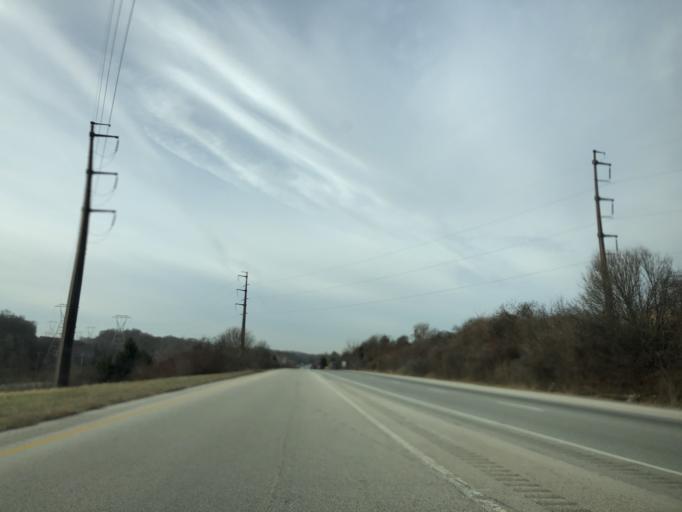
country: US
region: Pennsylvania
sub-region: Chester County
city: Exton
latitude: 40.0299
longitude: -75.5908
